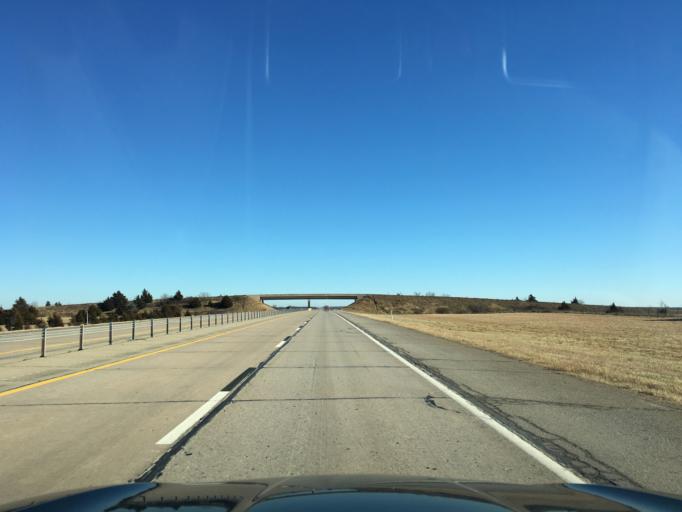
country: US
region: Oklahoma
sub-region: Pawnee County
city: Pawnee
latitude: 36.2254
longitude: -96.8758
